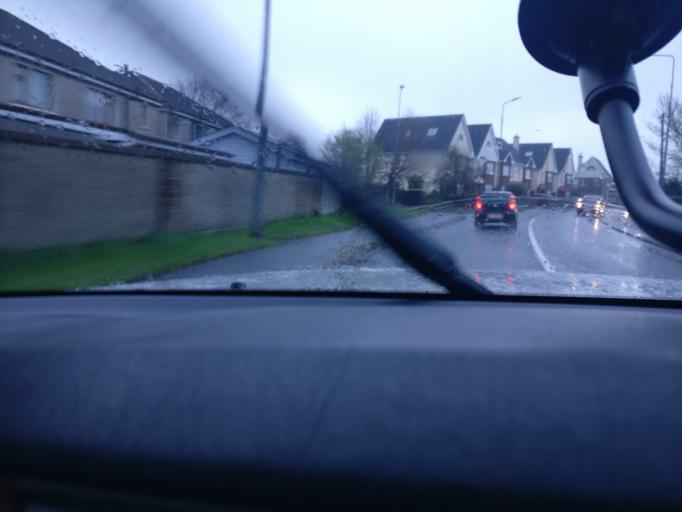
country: IE
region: Connaught
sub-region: County Galway
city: Gaillimh
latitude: 53.2907
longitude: -8.9960
